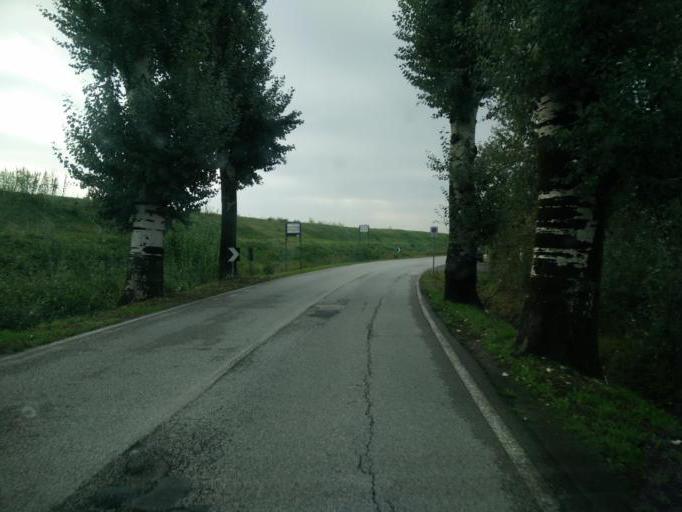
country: IT
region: Tuscany
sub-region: Province of Florence
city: Campi Bisenzio
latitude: 43.8473
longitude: 11.1257
